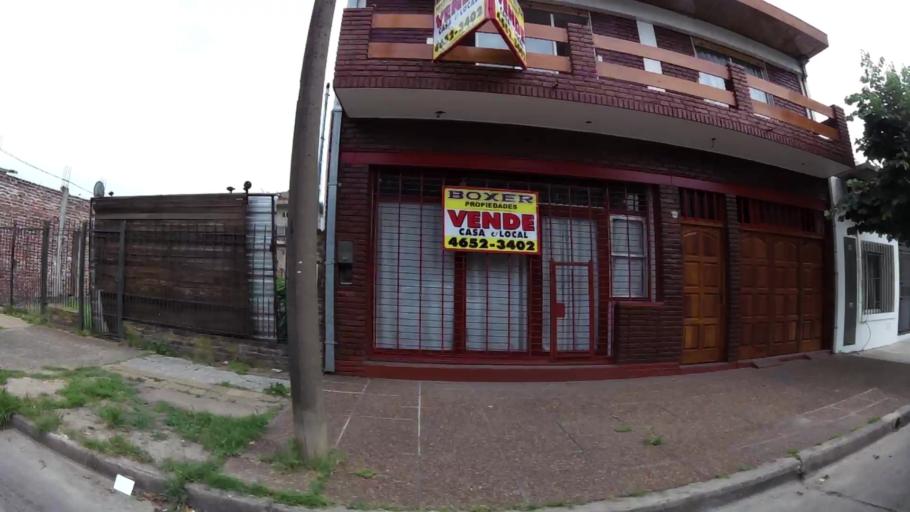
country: AR
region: Buenos Aires F.D.
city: Villa Lugano
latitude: -34.6860
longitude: -58.4990
